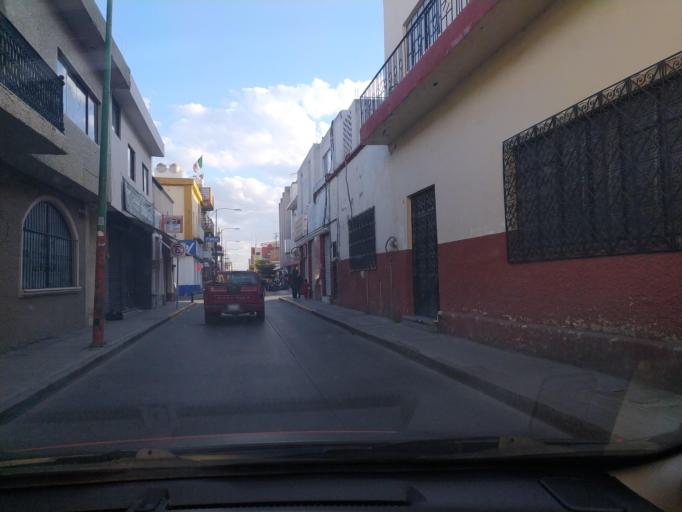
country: LA
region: Oudomxai
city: Muang La
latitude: 21.0195
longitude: 101.8577
